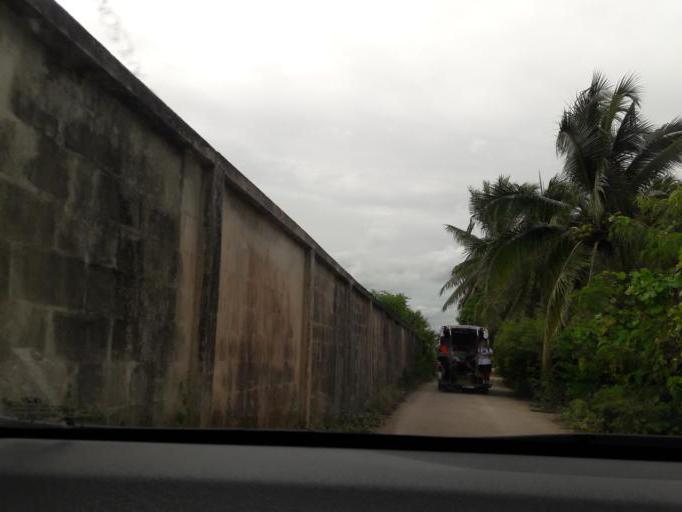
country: TH
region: Samut Sakhon
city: Ban Phaeo
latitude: 13.5575
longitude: 100.0405
